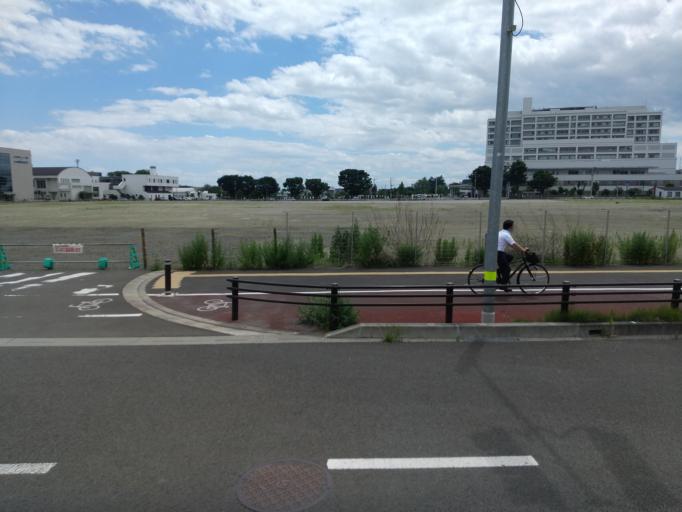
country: JP
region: Miyagi
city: Sendai-shi
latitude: 38.2624
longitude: 140.9081
